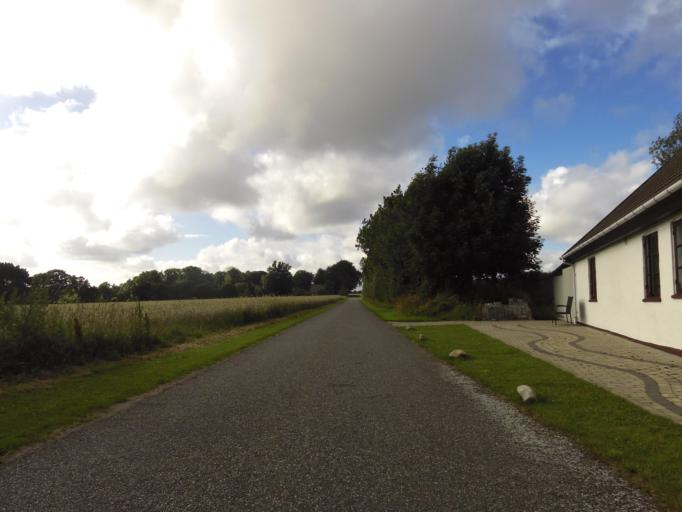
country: DK
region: South Denmark
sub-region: Tonder Kommune
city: Toftlund
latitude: 55.1285
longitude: 9.0782
